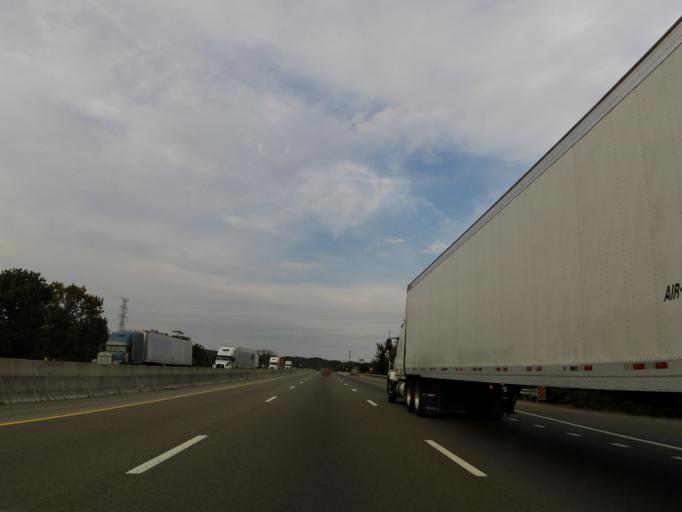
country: US
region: Tennessee
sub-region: Cheatham County
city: Pegram
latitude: 36.0790
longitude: -86.9604
